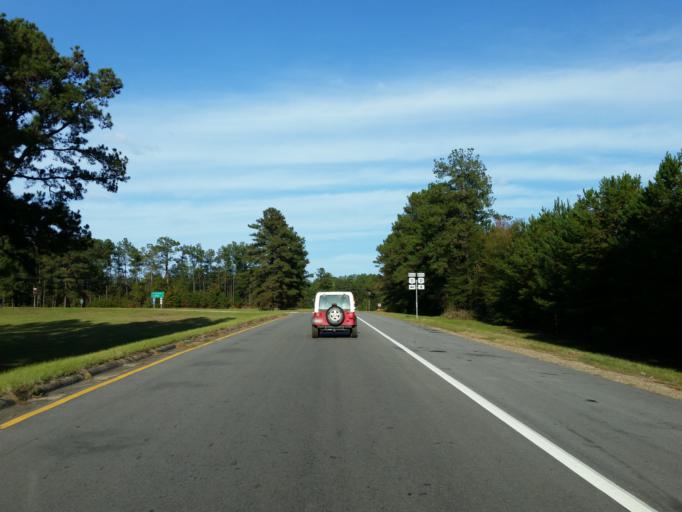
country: US
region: Mississippi
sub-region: Jones County
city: Laurel
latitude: 31.7209
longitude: -89.1029
